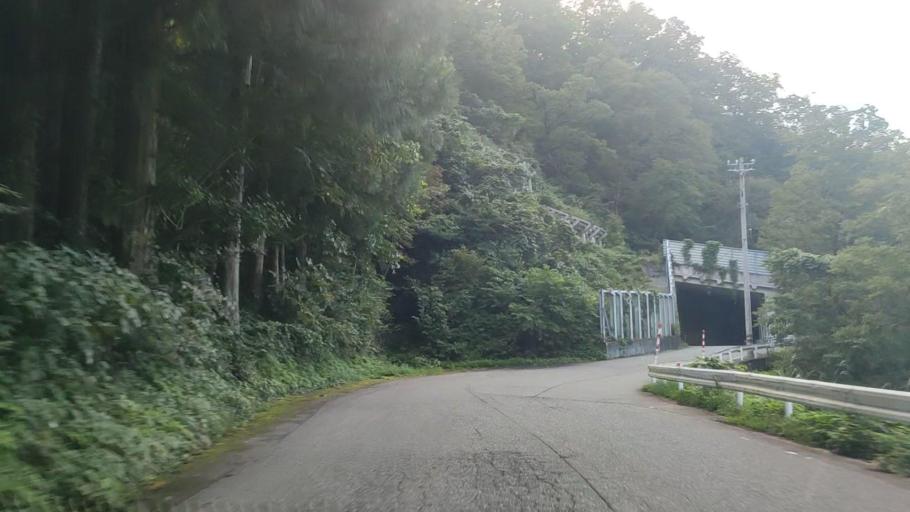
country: JP
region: Toyama
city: Yatsuomachi-higashikumisaka
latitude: 36.4838
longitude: 137.0676
